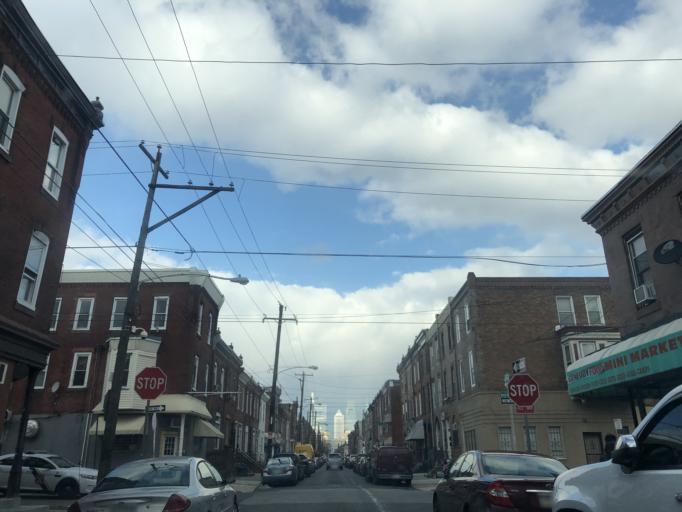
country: US
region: Pennsylvania
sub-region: Philadelphia County
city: Philadelphia
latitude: 39.9274
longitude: -75.1756
